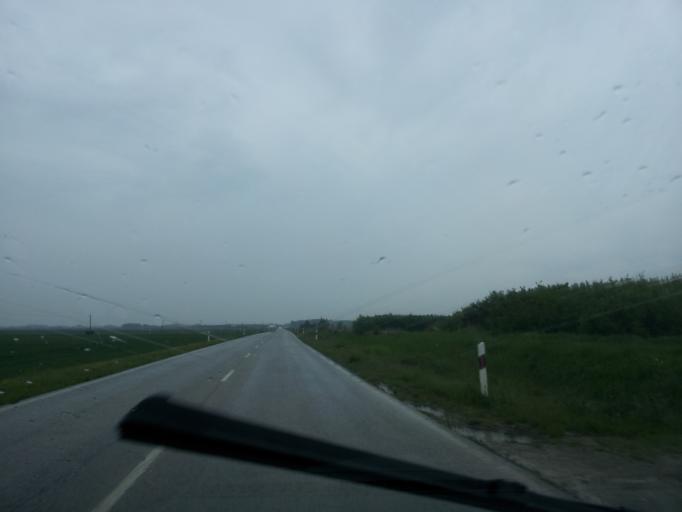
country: HU
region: Tolna
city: Szekszard
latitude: 46.3082
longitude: 18.7029
